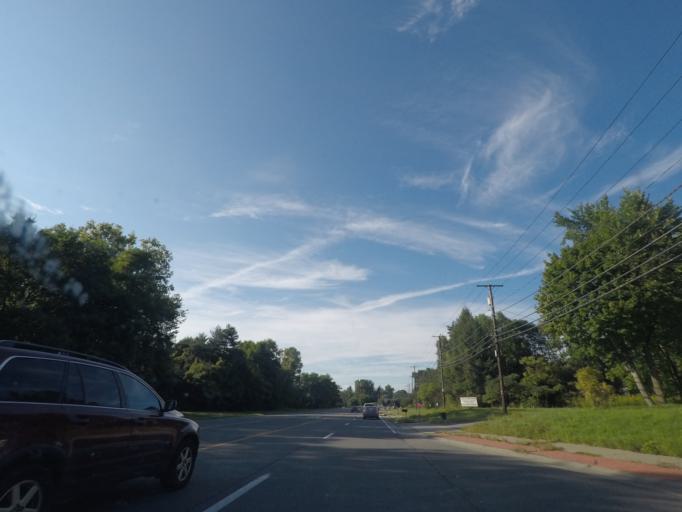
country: US
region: New York
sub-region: Schenectady County
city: Niskayuna
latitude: 42.7626
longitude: -73.8144
